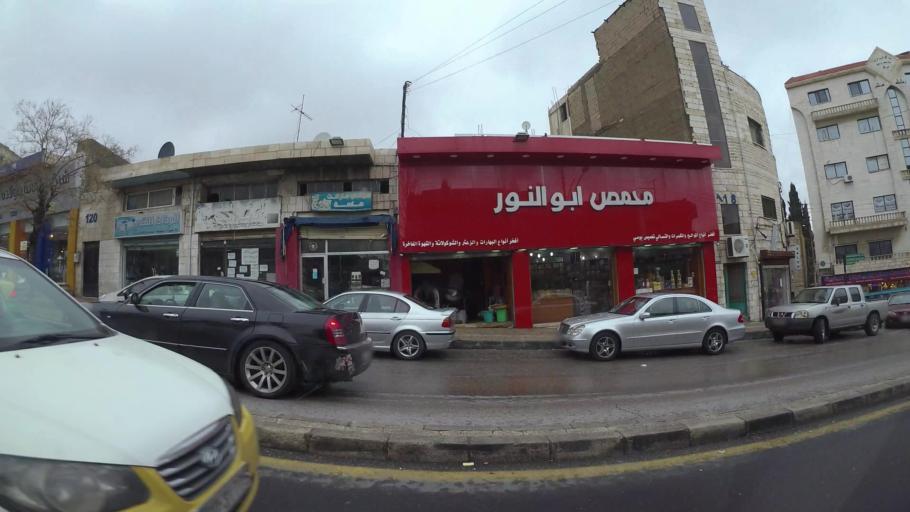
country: JO
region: Amman
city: Amman
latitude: 31.9631
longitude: 35.9236
